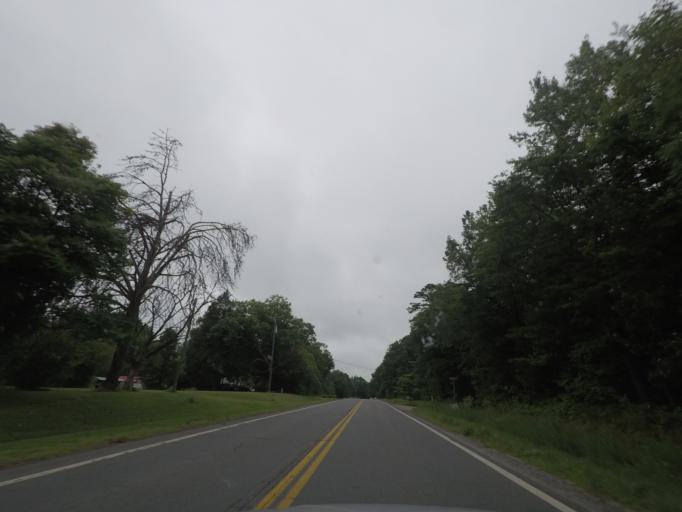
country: US
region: Virginia
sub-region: Fluvanna County
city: Weber City
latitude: 37.6853
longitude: -78.3287
